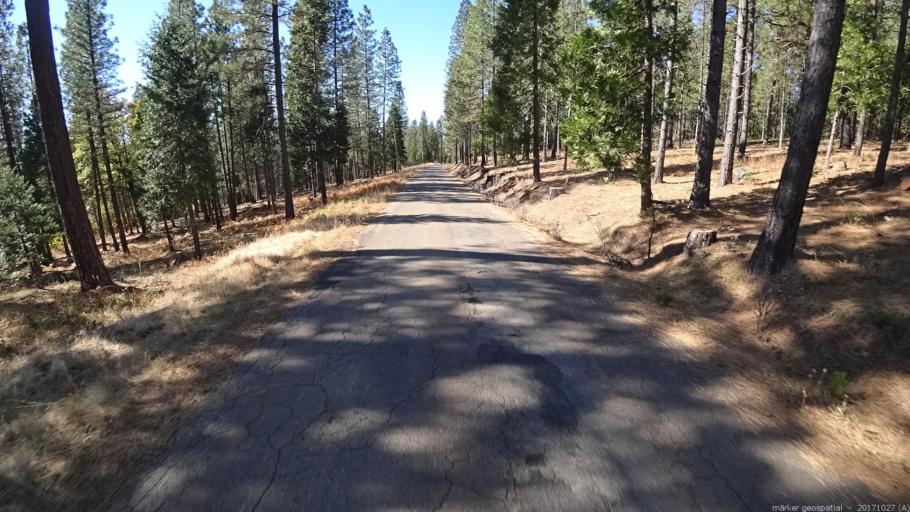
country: US
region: California
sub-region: Shasta County
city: Shingletown
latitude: 40.6141
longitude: -121.8341
